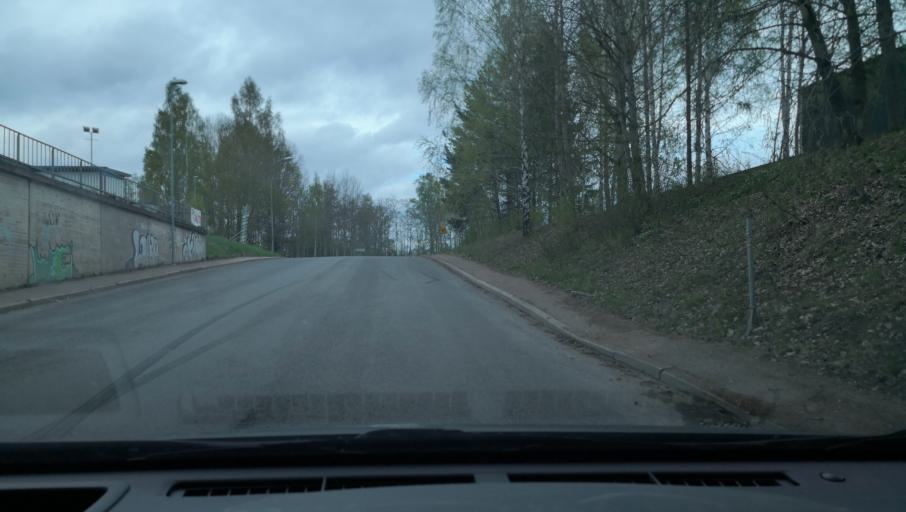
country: SE
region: Dalarna
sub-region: Avesta Kommun
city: Avesta
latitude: 60.1212
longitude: 16.2104
